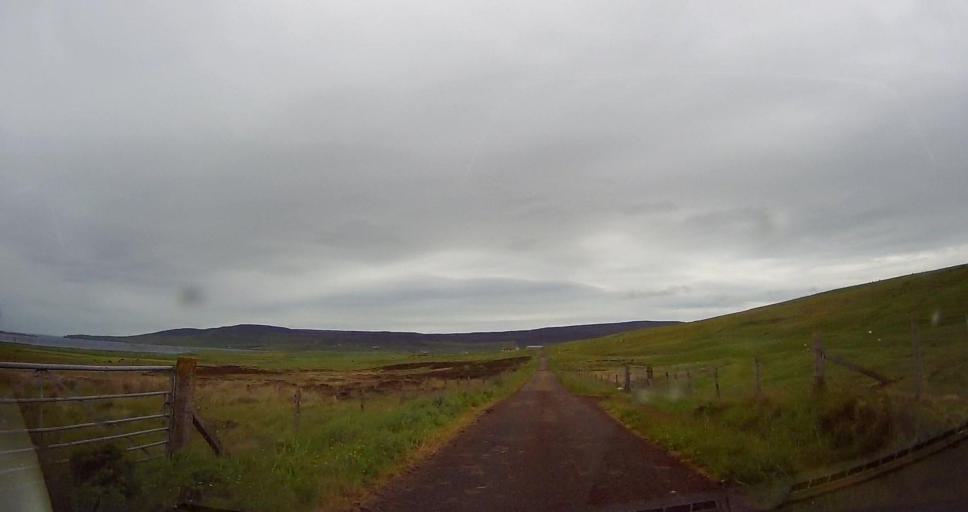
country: GB
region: Scotland
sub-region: Orkney Islands
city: Orkney
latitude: 59.1059
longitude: -3.0848
